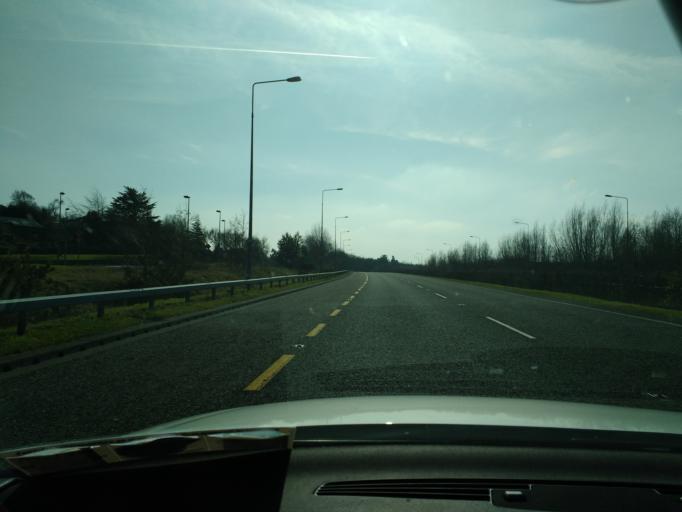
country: IE
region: Munster
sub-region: An Clar
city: Shannon
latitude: 52.7089
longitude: -8.8886
